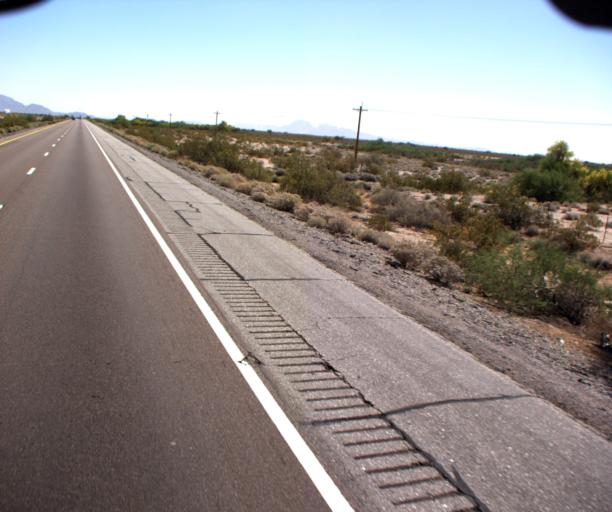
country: US
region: Arizona
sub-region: La Paz County
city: Salome
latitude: 33.5580
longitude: -113.2824
